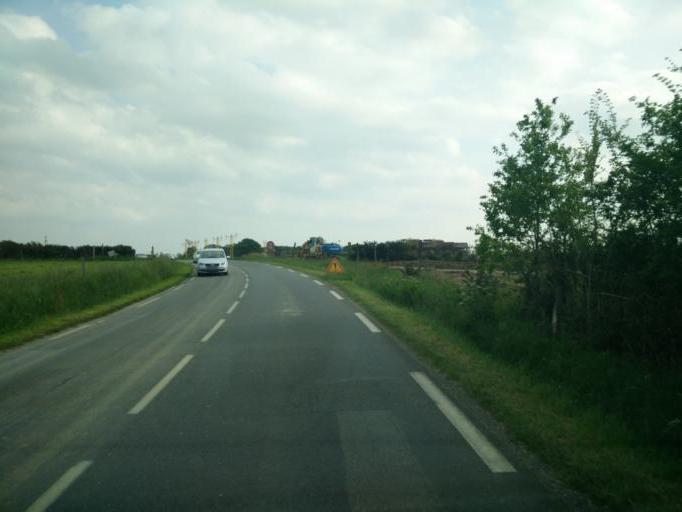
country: FR
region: Brittany
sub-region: Departement du Morbihan
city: Queven
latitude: 47.7649
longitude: -3.4252
